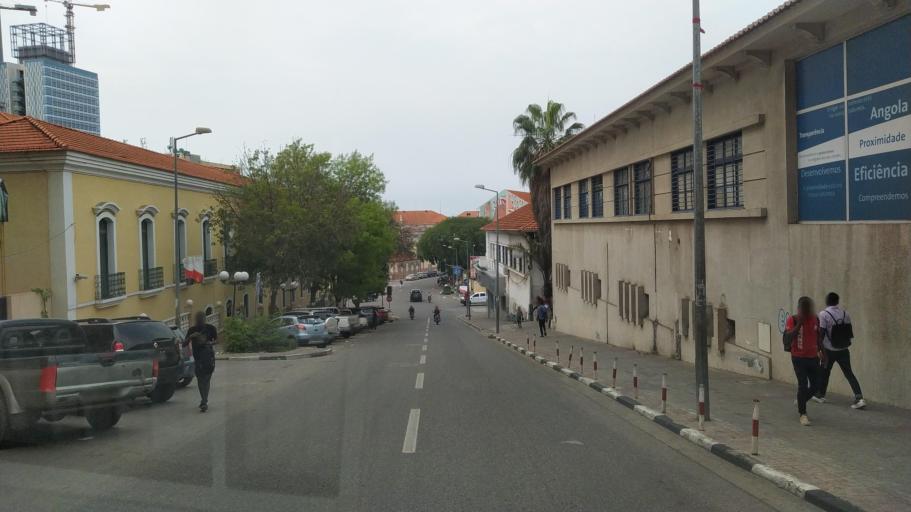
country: AO
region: Luanda
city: Luanda
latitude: -8.8140
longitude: 13.2349
